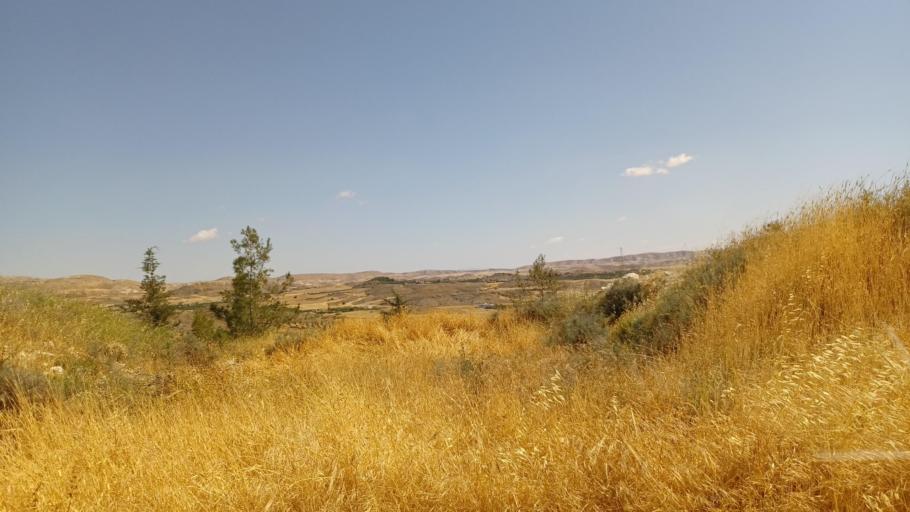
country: CY
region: Larnaka
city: Aradippou
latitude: 34.9939
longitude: 33.5695
